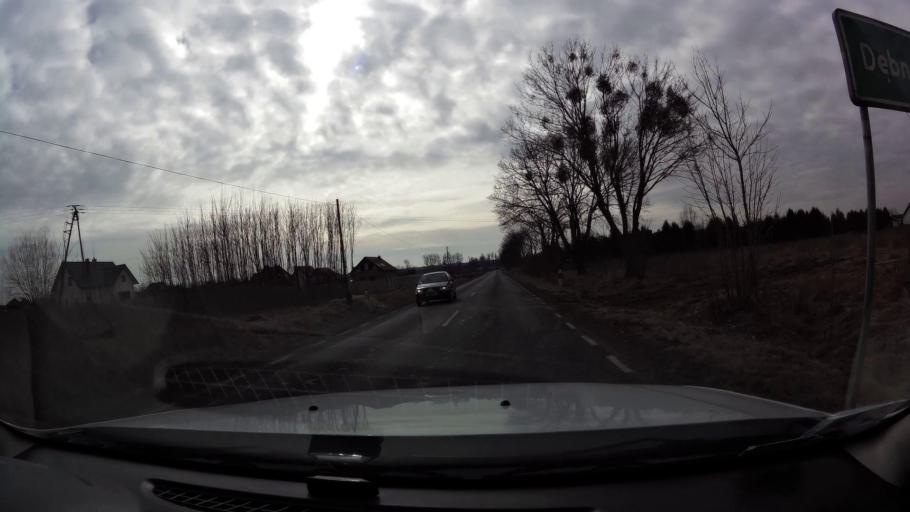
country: PL
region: West Pomeranian Voivodeship
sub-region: Powiat mysliborski
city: Debno
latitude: 52.7516
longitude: 14.6893
